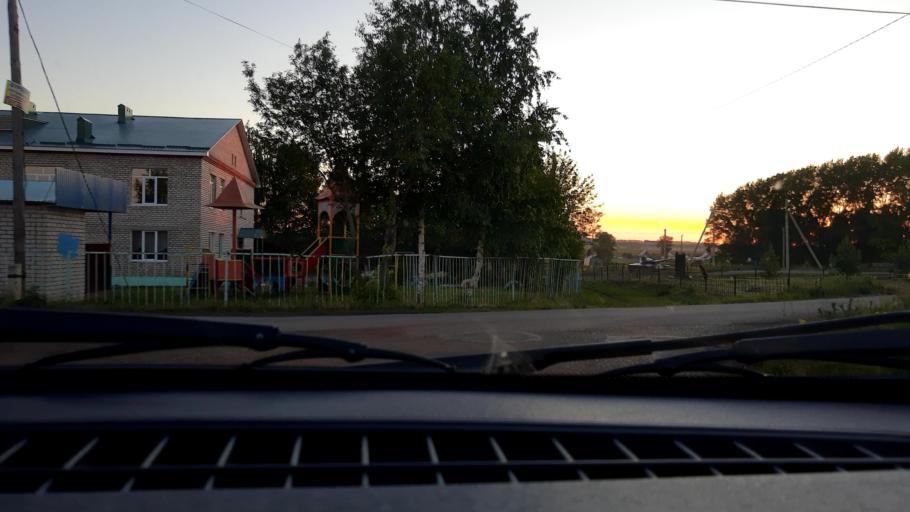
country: RU
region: Bashkortostan
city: Asanovo
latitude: 54.8884
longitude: 55.6243
